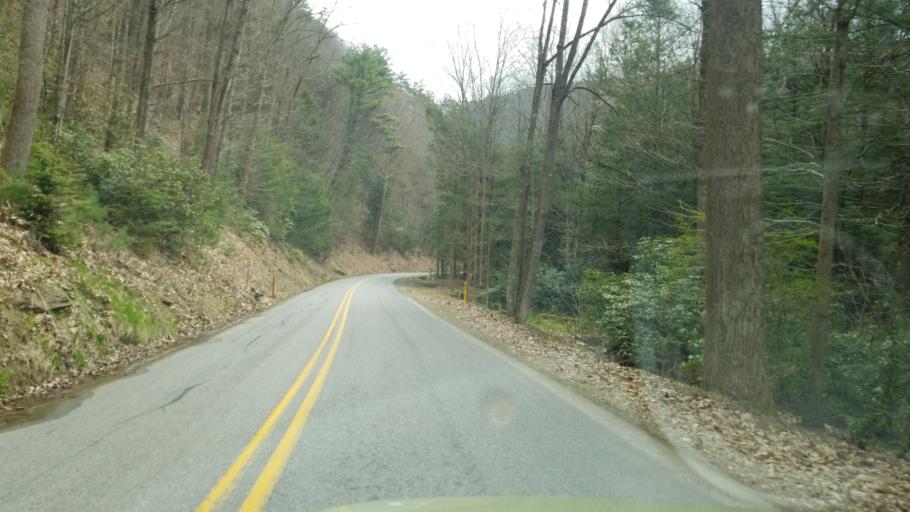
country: US
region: Pennsylvania
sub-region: Cameron County
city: Emporium
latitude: 41.2828
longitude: -78.1317
